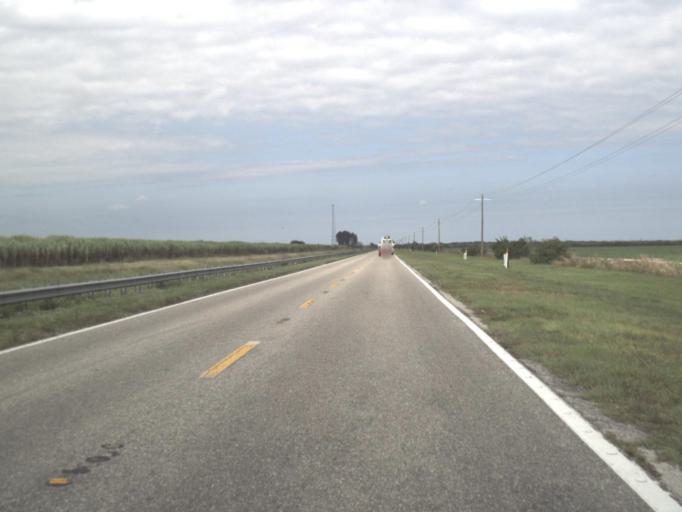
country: US
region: Florida
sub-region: Glades County
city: Moore Haven
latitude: 26.7569
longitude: -81.1533
